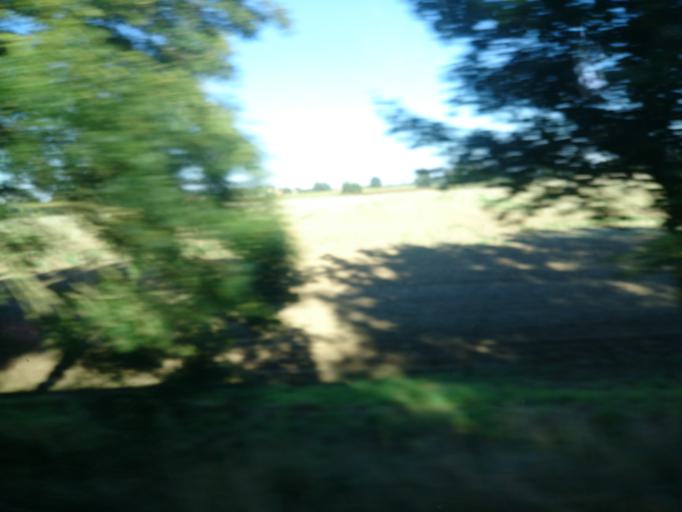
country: DE
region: Mecklenburg-Vorpommern
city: Ducherow
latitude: 53.8010
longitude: 13.7402
